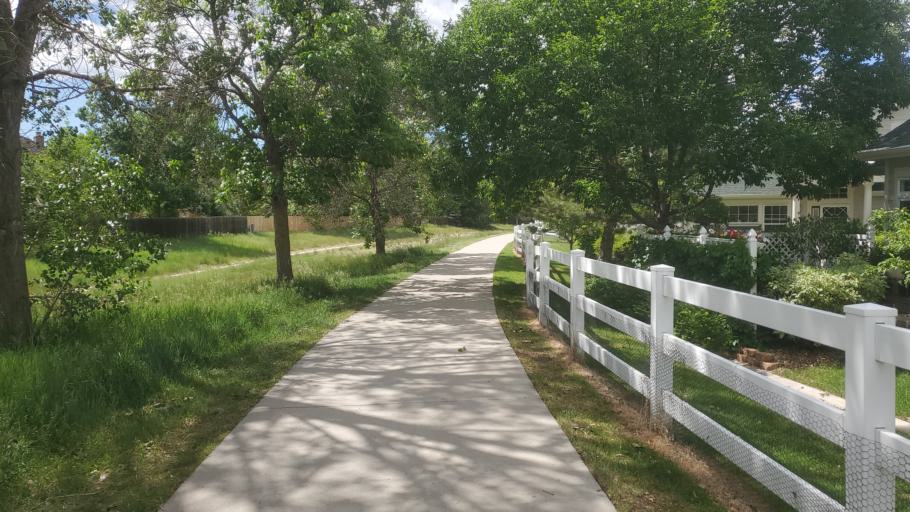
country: US
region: Colorado
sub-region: Adams County
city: Aurora
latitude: 39.6697
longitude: -104.8409
